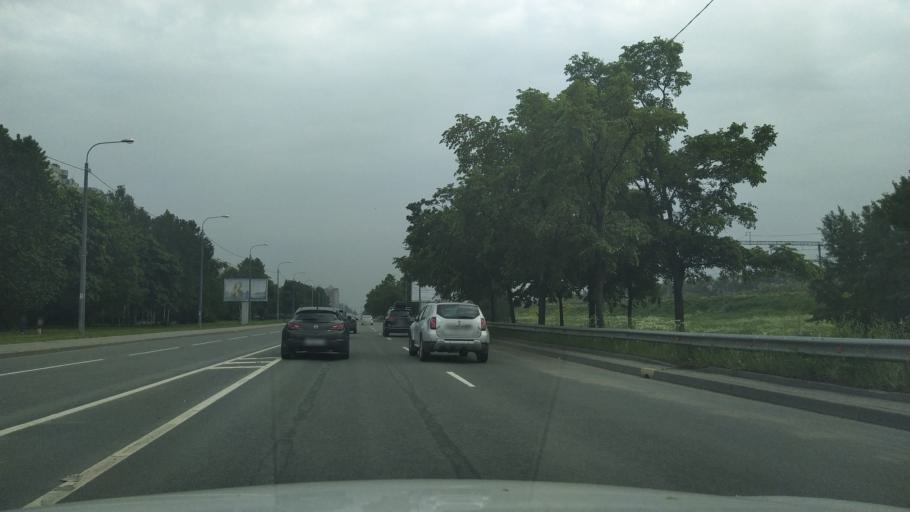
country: RU
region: St.-Petersburg
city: Kupchino
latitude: 59.8716
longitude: 30.3571
